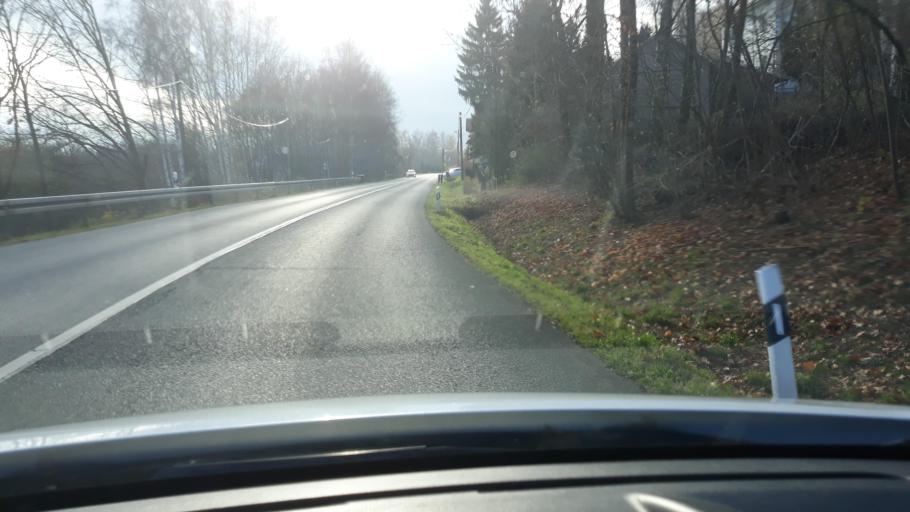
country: DE
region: Saxony
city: Wilkau-Hasslau
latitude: 50.6523
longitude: 12.5228
